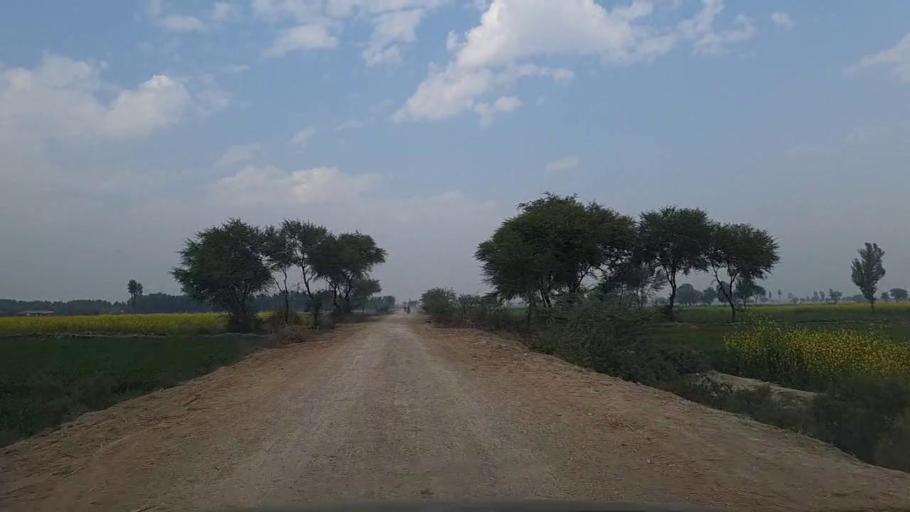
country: PK
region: Sindh
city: Daur
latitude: 26.3671
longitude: 68.3897
